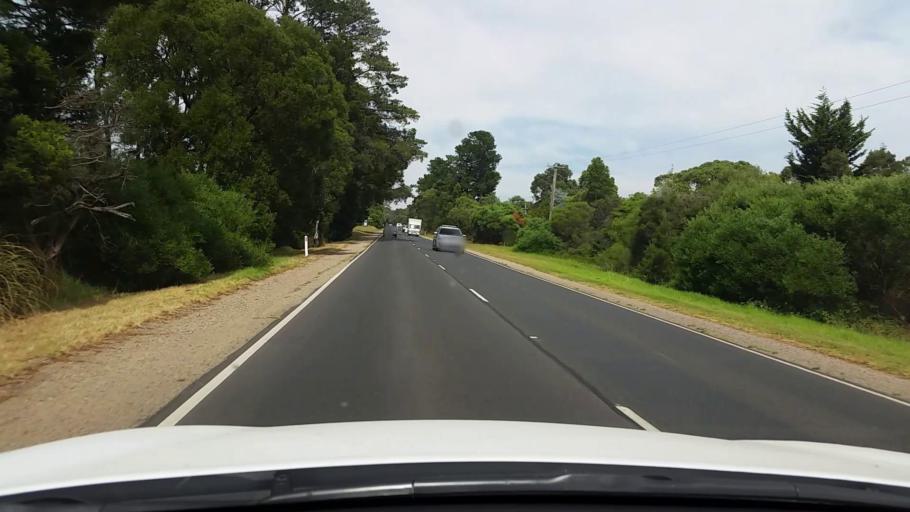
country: AU
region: Victoria
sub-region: Mornington Peninsula
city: Balnarring
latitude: -38.3692
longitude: 145.1335
